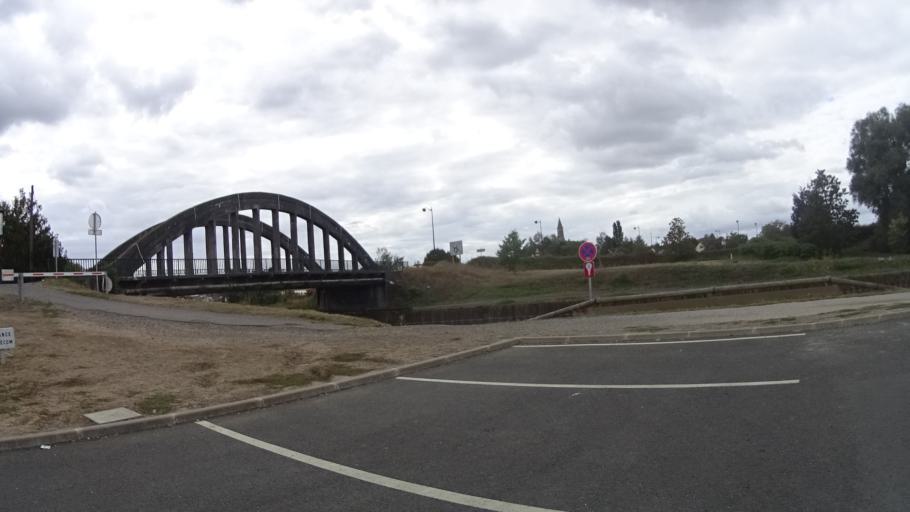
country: FR
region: Picardie
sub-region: Departement de l'Aisne
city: Beautor
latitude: 49.6620
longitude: 3.3512
